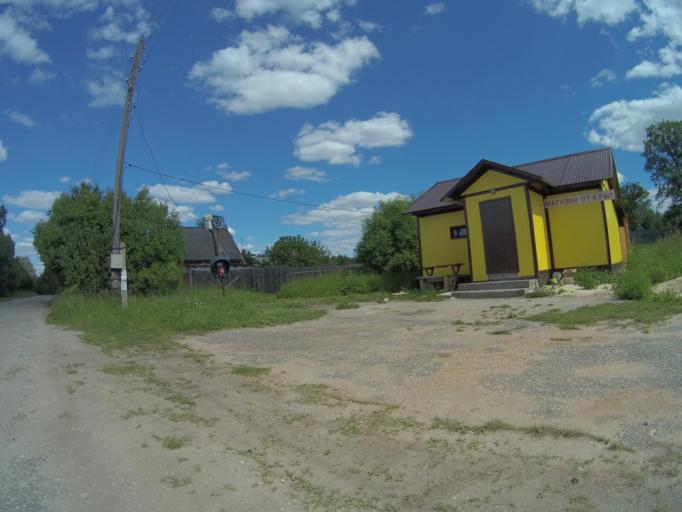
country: RU
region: Vladimir
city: Sudogda
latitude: 56.0390
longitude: 40.8777
